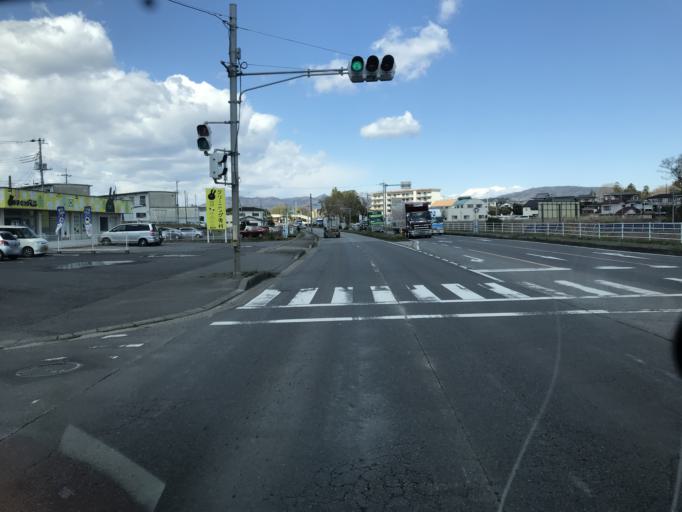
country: JP
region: Ibaraki
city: Naka
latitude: 36.1127
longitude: 140.1938
